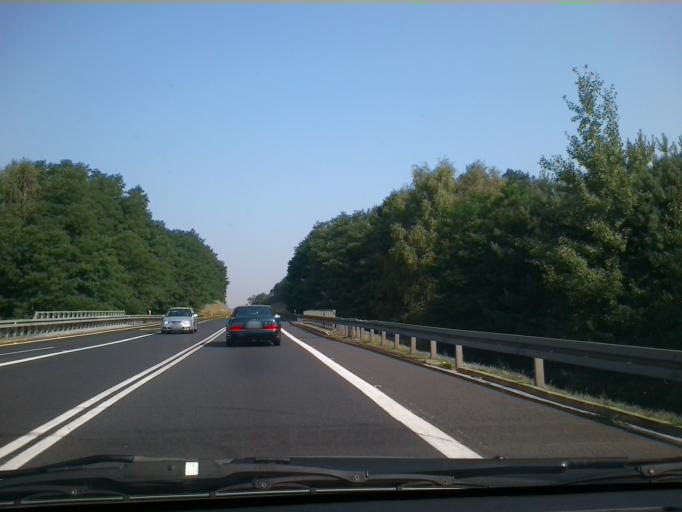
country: PL
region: Lubusz
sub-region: Zielona Gora
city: Zielona Gora
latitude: 51.9060
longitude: 15.5873
